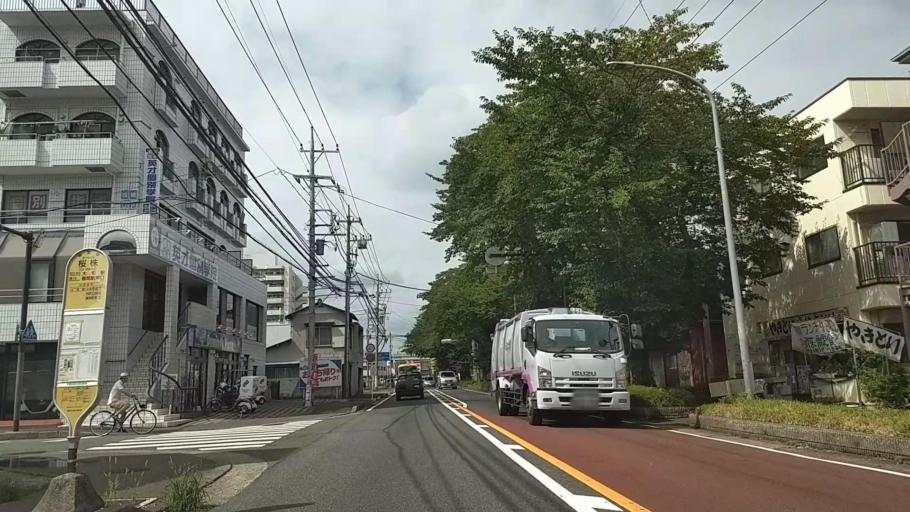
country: JP
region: Kanagawa
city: Minami-rinkan
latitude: 35.4497
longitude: 139.4677
